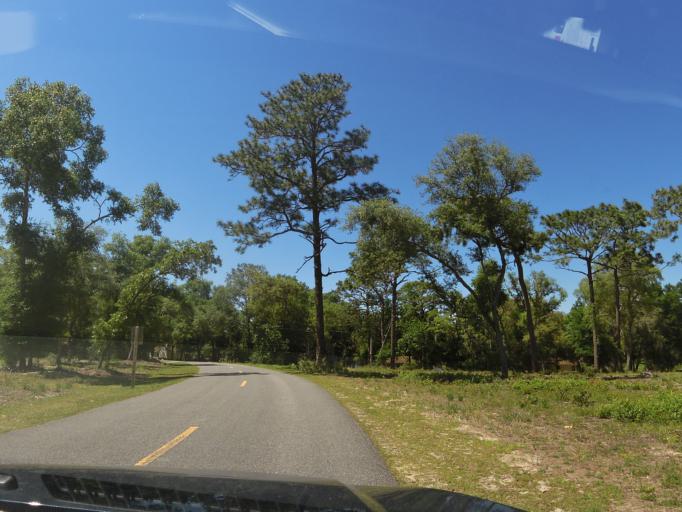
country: US
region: Florida
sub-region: Clay County
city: Keystone Heights
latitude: 29.8222
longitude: -81.9466
